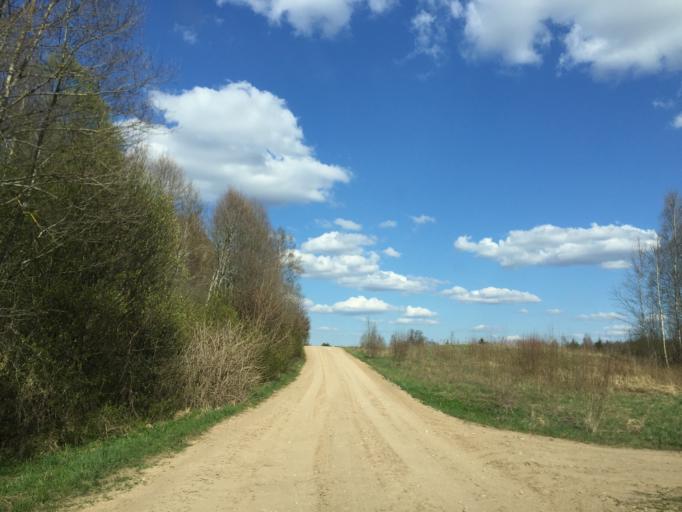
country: LV
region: Krimulda
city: Ragana
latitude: 57.3437
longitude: 24.6923
